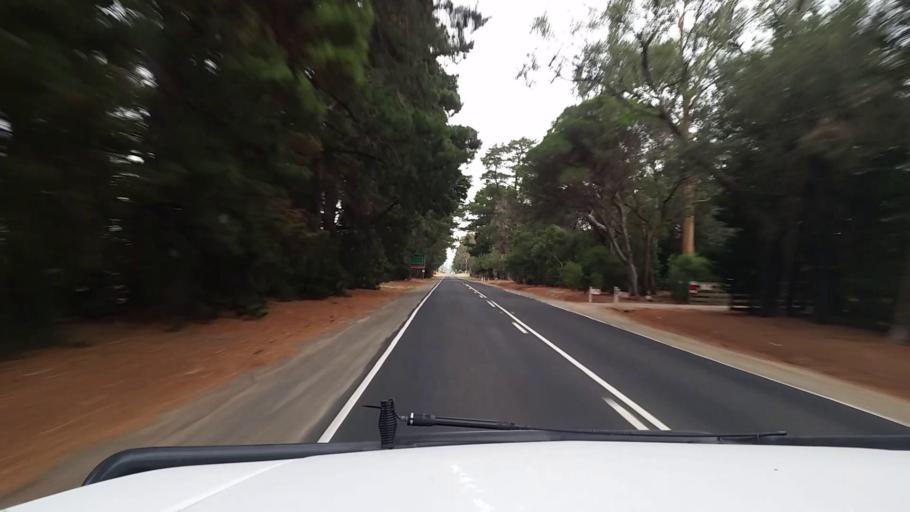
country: AU
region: Victoria
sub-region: Mornington Peninsula
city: Somerville
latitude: -38.2242
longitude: 145.1540
